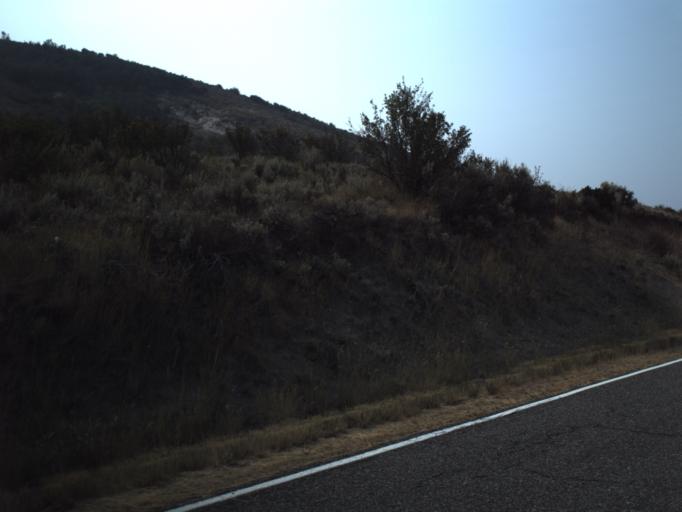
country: US
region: Utah
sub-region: Morgan County
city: Morgan
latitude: 40.9688
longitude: -111.5421
